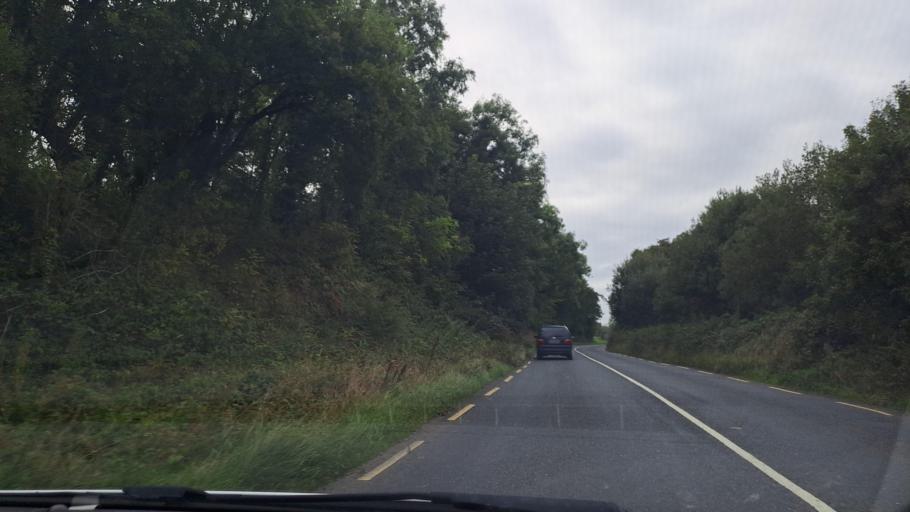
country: IE
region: Ulster
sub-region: County Monaghan
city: Carrickmacross
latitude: 54.0012
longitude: -6.7363
